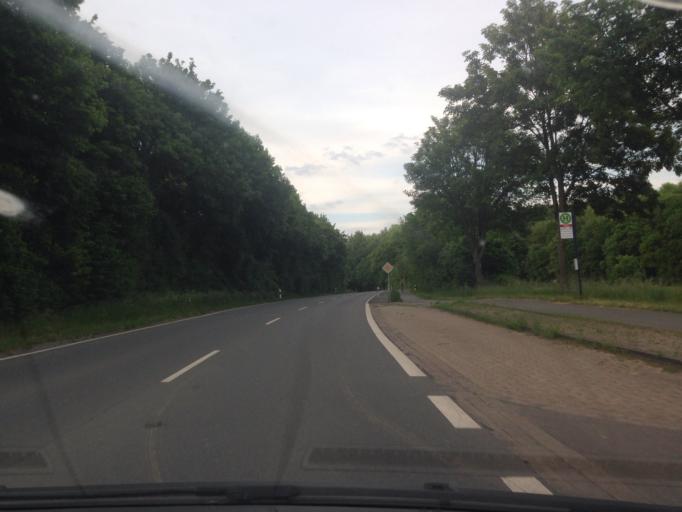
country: DE
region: North Rhine-Westphalia
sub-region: Regierungsbezirk Munster
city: Muenster
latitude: 52.0061
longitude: 7.5579
